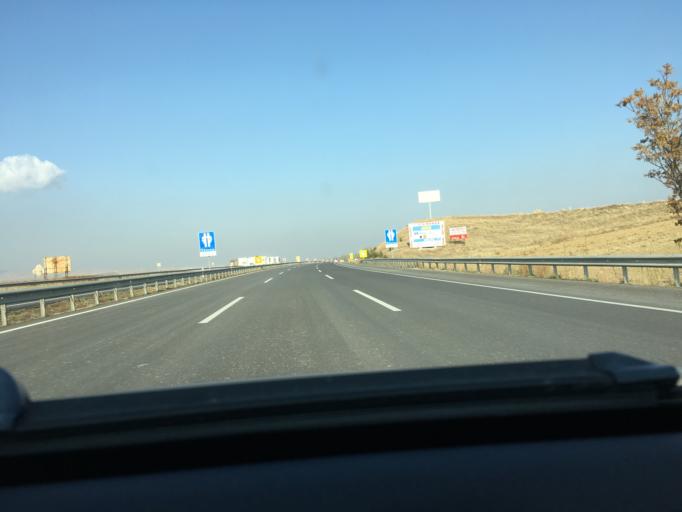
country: TR
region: Ankara
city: Temelli
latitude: 39.6786
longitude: 32.2377
